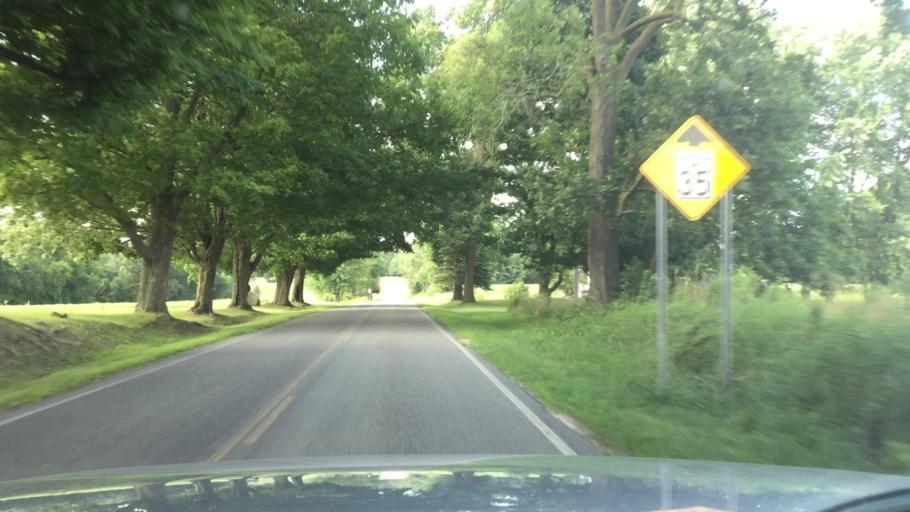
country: US
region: Michigan
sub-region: Ionia County
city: Belding
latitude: 43.0750
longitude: -85.2281
